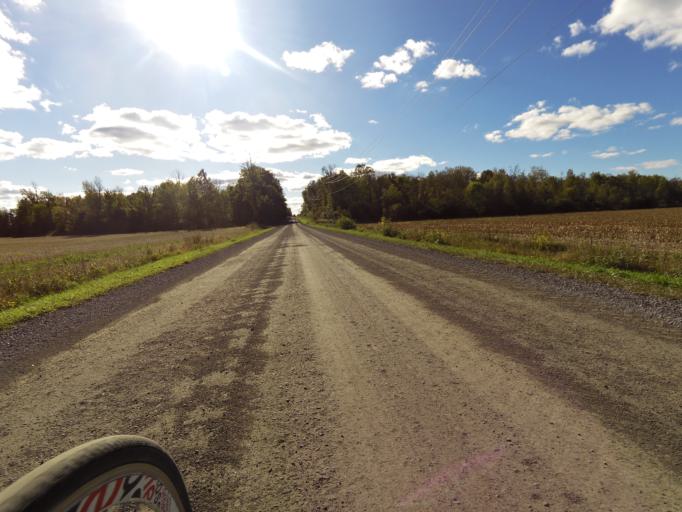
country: CA
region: Ontario
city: Bells Corners
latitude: 45.1303
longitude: -75.6665
